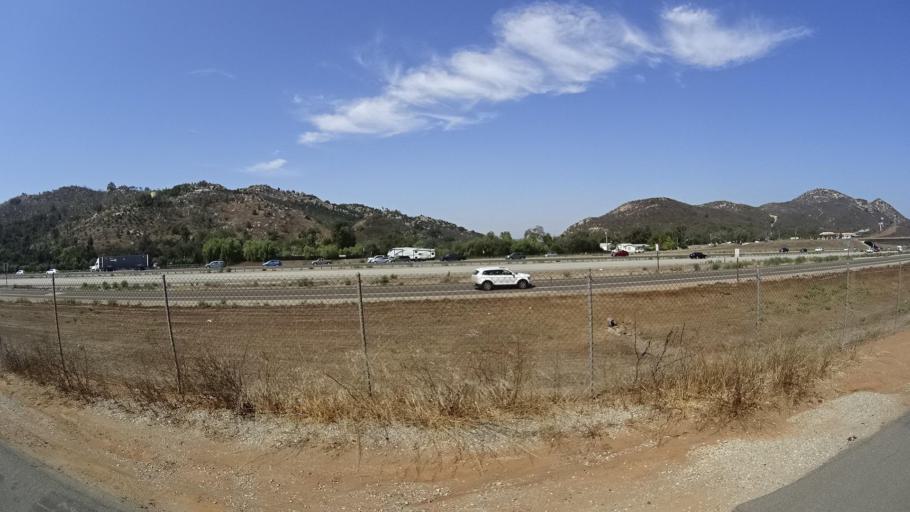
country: US
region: California
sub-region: San Diego County
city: Hidden Meadows
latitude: 33.1952
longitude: -117.1228
